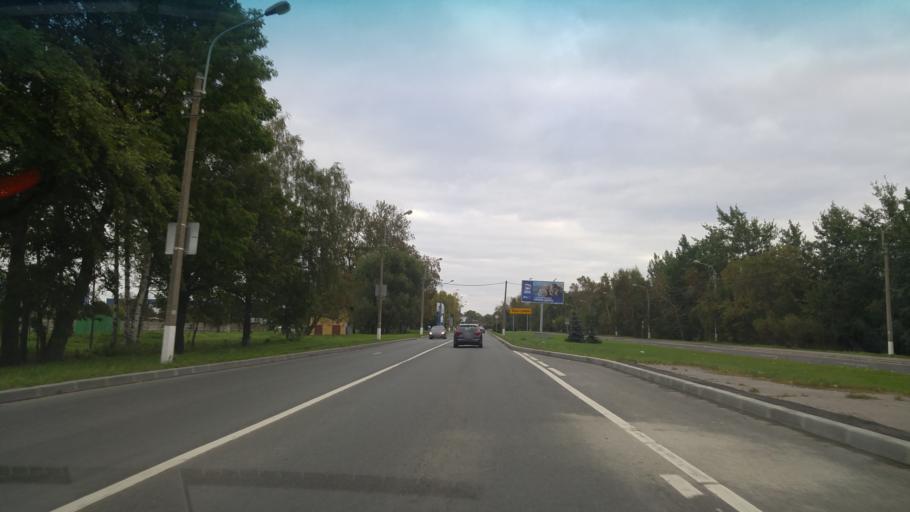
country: RU
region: St.-Petersburg
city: Kronshtadt
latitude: 60.0088
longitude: 29.7339
